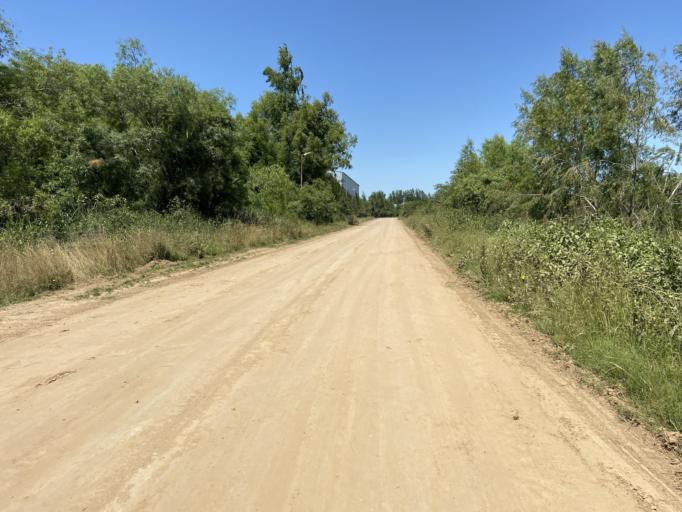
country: AR
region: Entre Rios
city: Villa Paranacito
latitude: -33.7050
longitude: -58.6366
